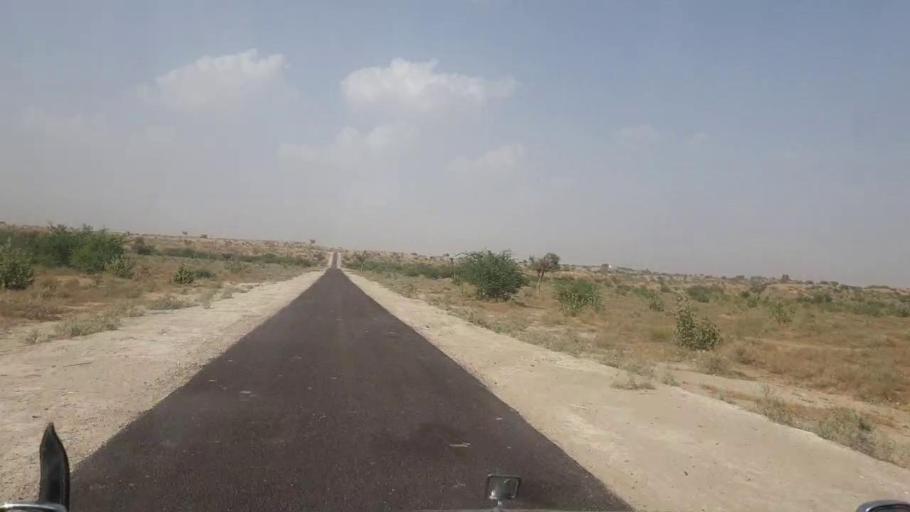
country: PK
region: Sindh
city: Islamkot
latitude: 25.2045
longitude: 70.2834
